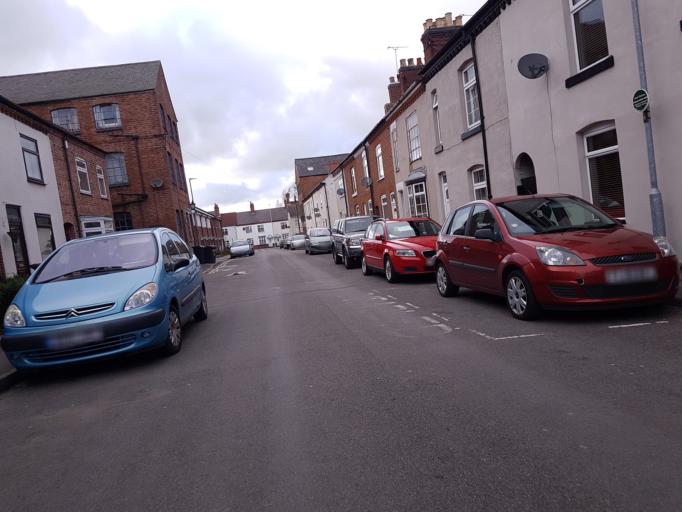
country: GB
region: England
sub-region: Leicestershire
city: Earl Shilton
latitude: 52.5737
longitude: -1.3219
